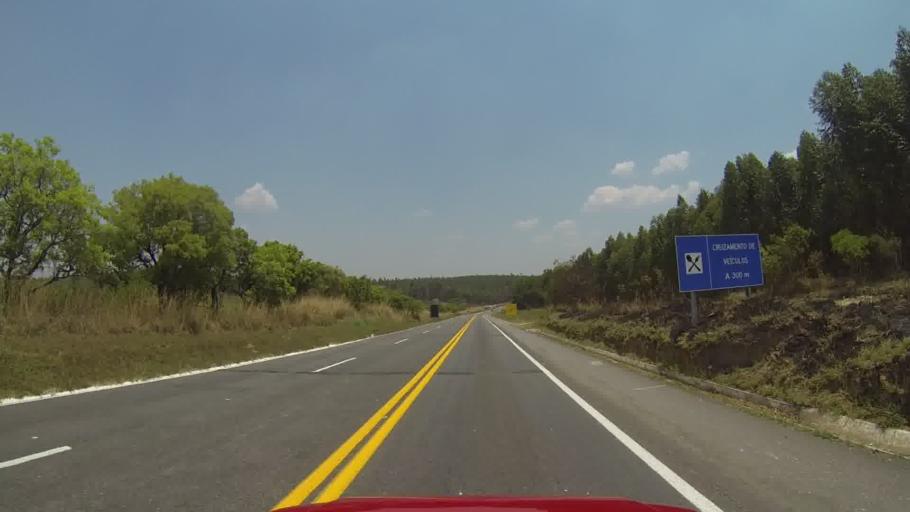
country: BR
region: Minas Gerais
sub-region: Formiga
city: Formiga
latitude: -20.3497
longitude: -45.3316
